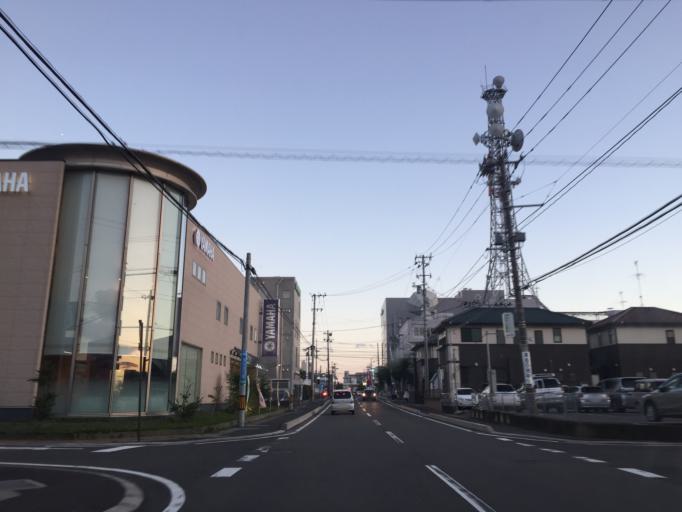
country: JP
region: Fukushima
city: Koriyama
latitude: 37.4090
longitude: 140.3566
